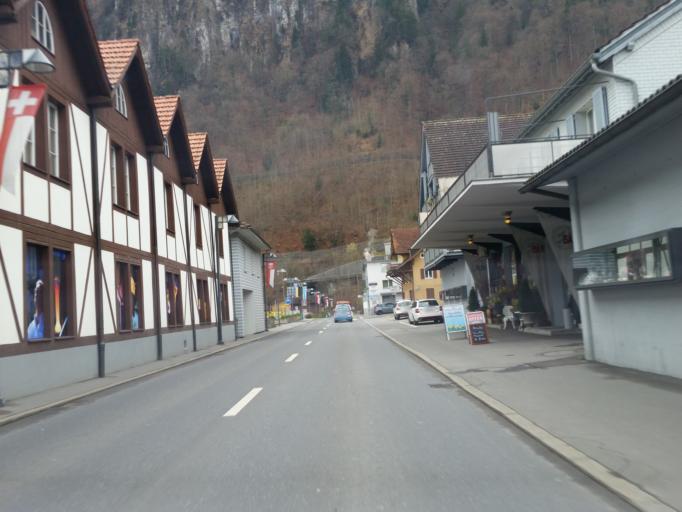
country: CH
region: Nidwalden
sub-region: Nidwalden
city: Hergiswil
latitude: 46.9821
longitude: 8.3113
